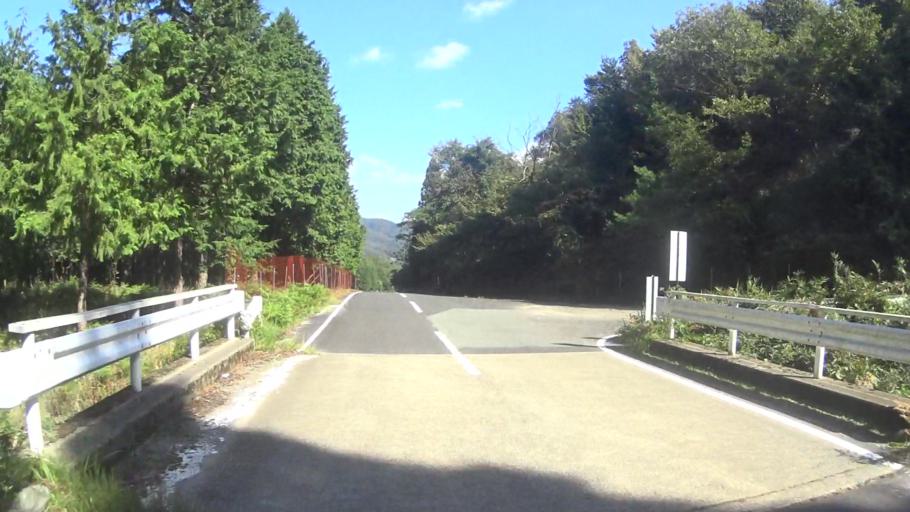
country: JP
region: Hyogo
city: Toyooka
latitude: 35.5342
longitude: 134.9282
